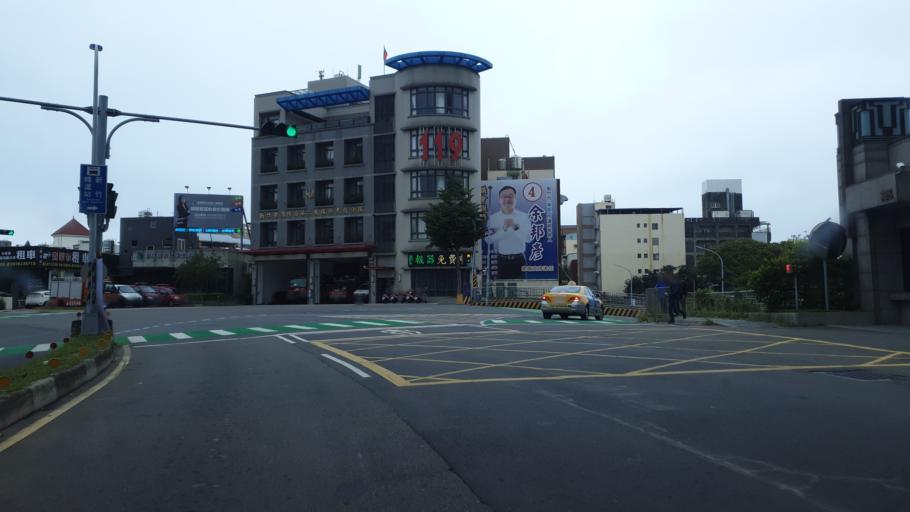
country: TW
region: Taiwan
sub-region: Hsinchu
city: Hsinchu
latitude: 24.8007
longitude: 120.9758
